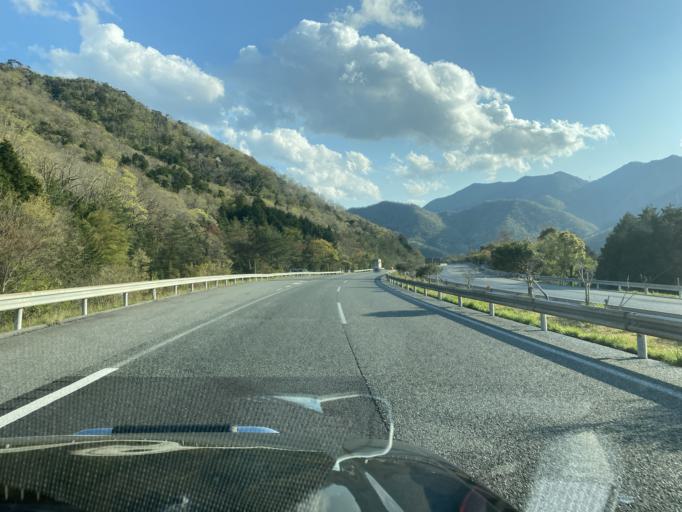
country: JP
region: Hyogo
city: Sasayama
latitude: 35.0039
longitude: 135.1586
